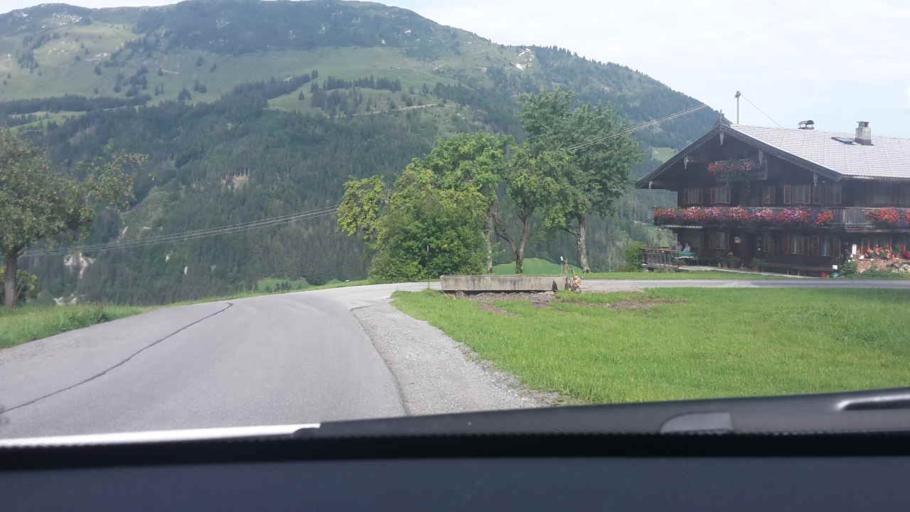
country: AT
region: Tyrol
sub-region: Politischer Bezirk Kitzbuhel
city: Kirchberg in Tirol
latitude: 47.4201
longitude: 12.3244
